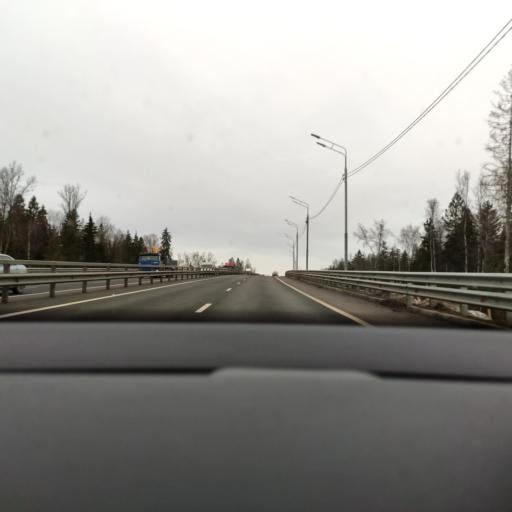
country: RU
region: Moskovskaya
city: Zvenigorod
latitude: 55.6783
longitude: 36.8979
